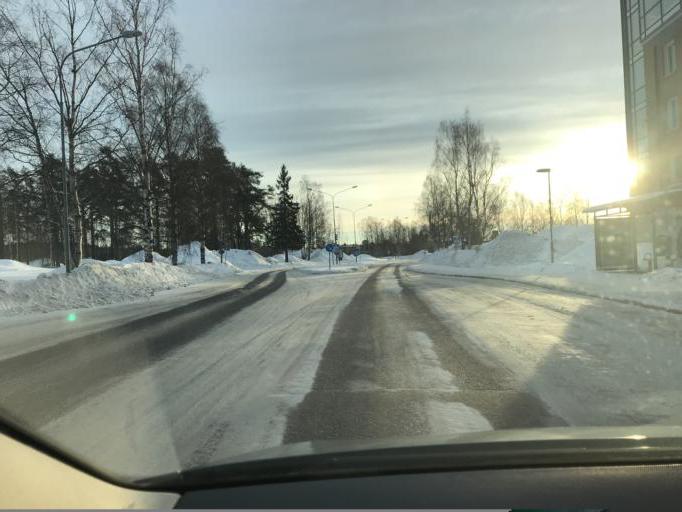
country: SE
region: Norrbotten
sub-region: Lulea Kommun
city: Lulea
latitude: 65.6018
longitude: 22.1289
